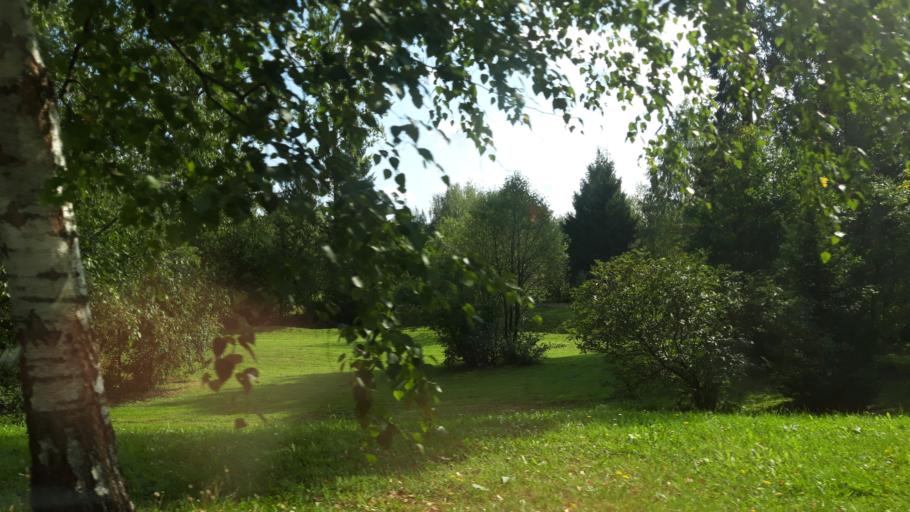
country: RU
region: Moskovskaya
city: Mendeleyevo
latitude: 56.0474
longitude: 37.2167
